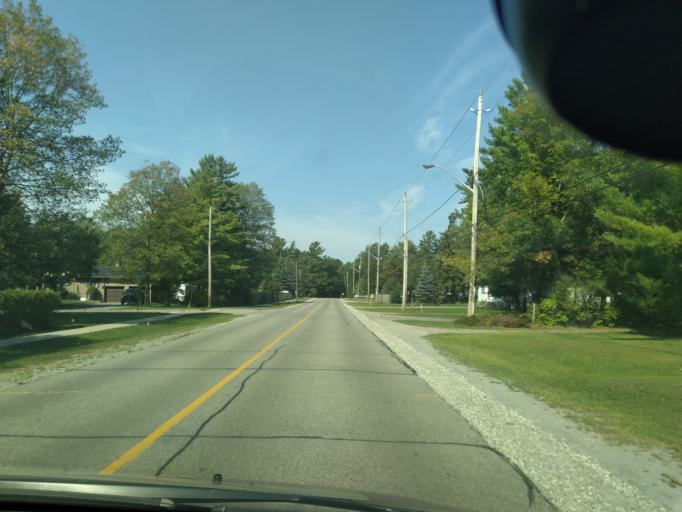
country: CA
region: Ontario
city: Newmarket
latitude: 44.1197
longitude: -79.5060
